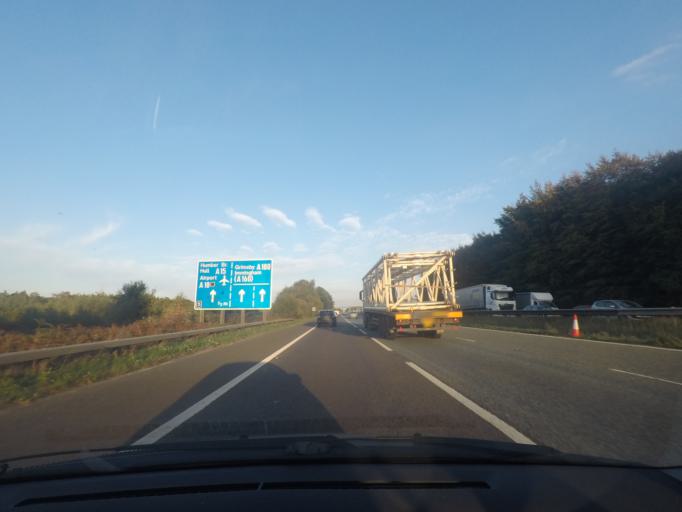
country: GB
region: England
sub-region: North Lincolnshire
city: Barnetby le Wold
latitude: 53.5824
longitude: -0.4341
